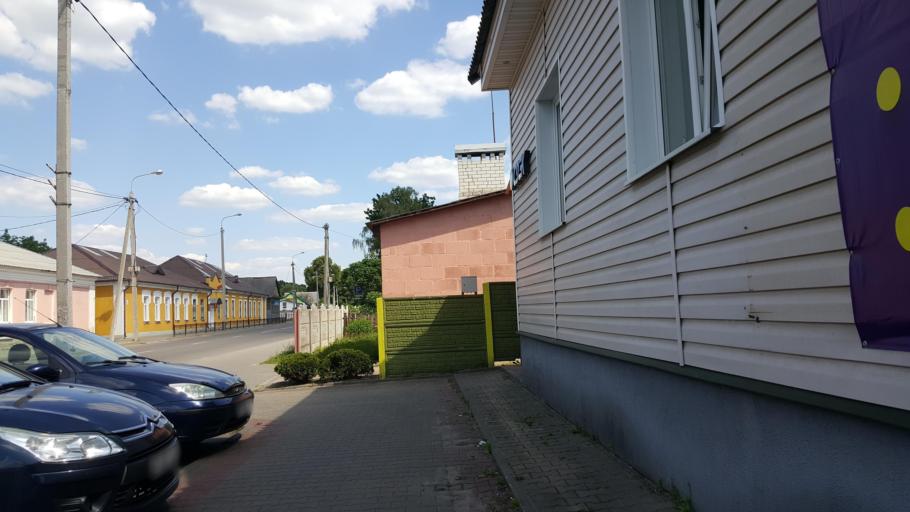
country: BY
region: Brest
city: Horad Kobryn
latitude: 52.2121
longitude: 24.3635
